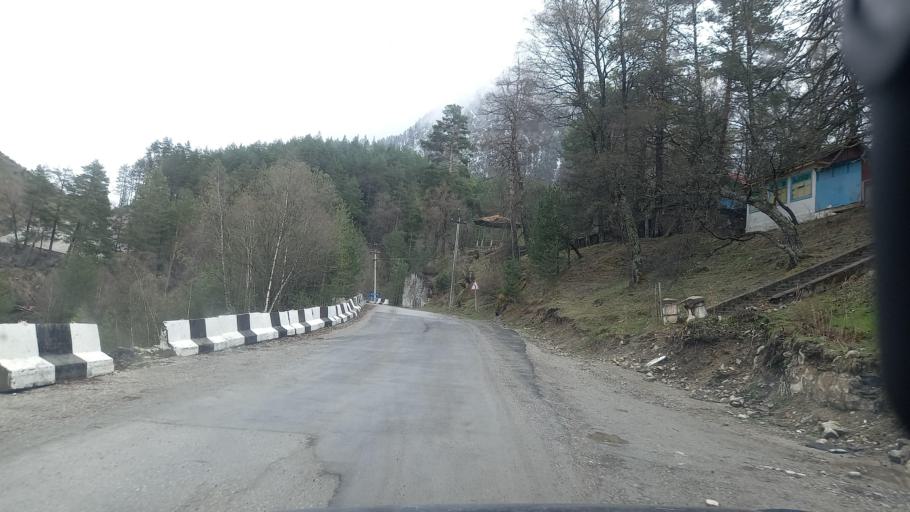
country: RU
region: Kabardino-Balkariya
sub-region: El'brusskiy Rayon
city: El'brus
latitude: 43.2296
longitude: 42.6537
